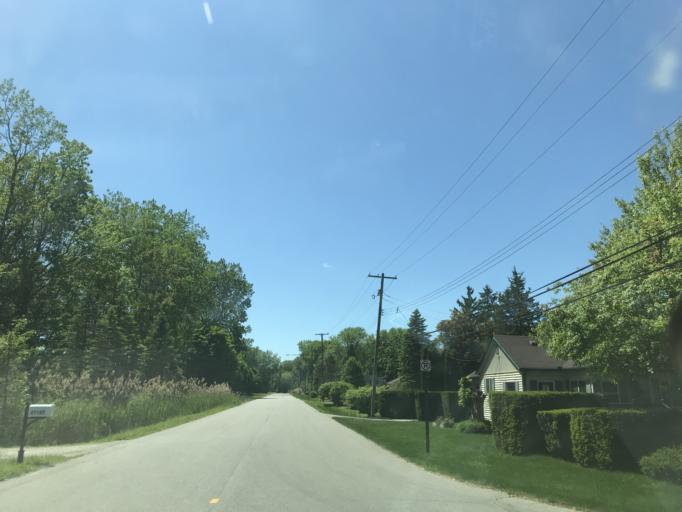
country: US
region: Michigan
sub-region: Wayne County
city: Woodhaven
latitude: 42.1740
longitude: -83.2997
